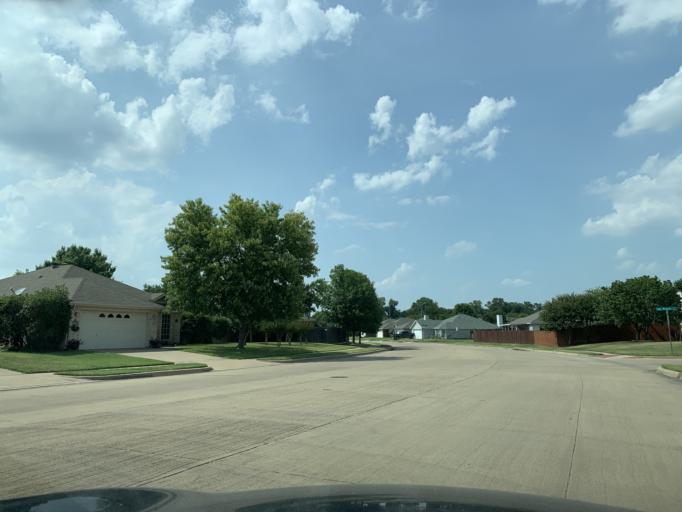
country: US
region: Texas
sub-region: Tarrant County
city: Hurst
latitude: 32.8036
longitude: -97.1902
